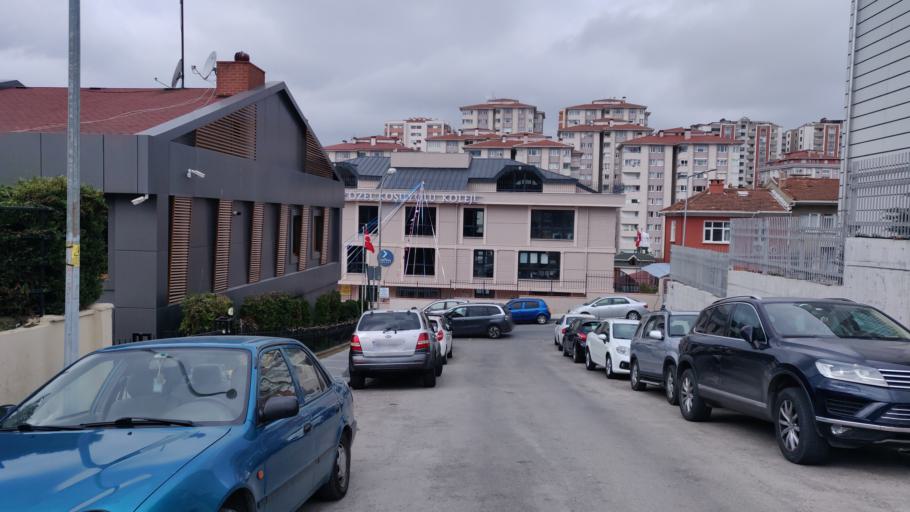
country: TR
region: Istanbul
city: UEskuedar
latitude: 41.0091
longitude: 29.0357
